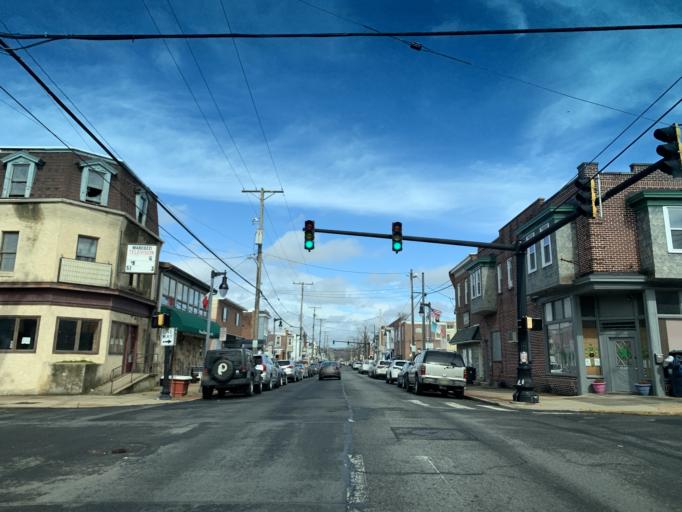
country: US
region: Delaware
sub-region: New Castle County
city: Wilmington
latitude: 39.7497
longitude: -75.5710
